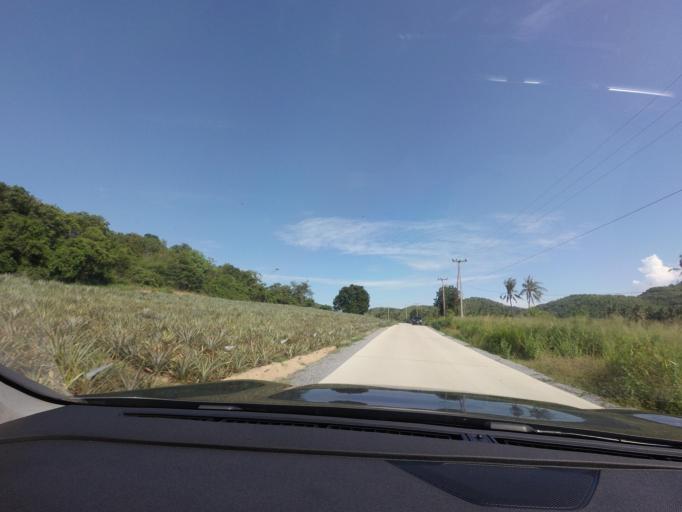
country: TH
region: Prachuap Khiri Khan
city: Pran Buri
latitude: 12.4736
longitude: 99.9378
